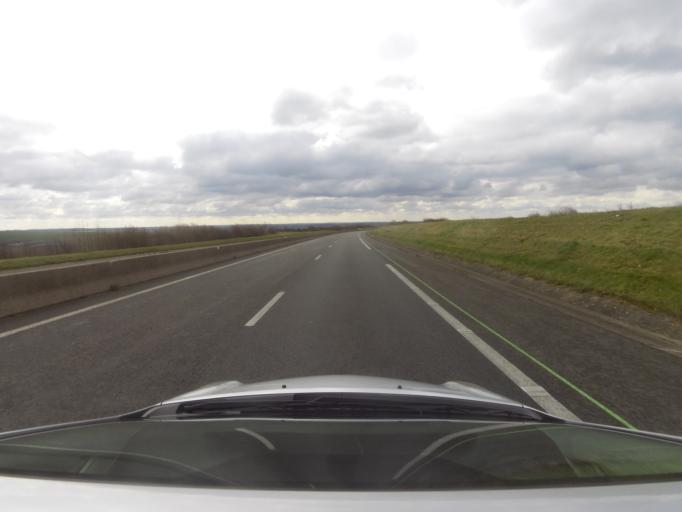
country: FR
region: Nord-Pas-de-Calais
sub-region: Departement du Pas-de-Calais
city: Etaples
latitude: 50.5469
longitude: 1.6759
